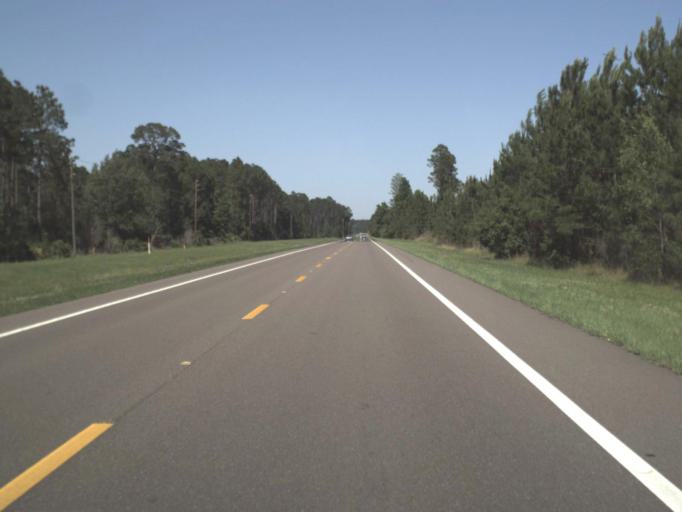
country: US
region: Florida
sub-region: Duval County
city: Baldwin
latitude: 30.2971
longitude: -82.0387
